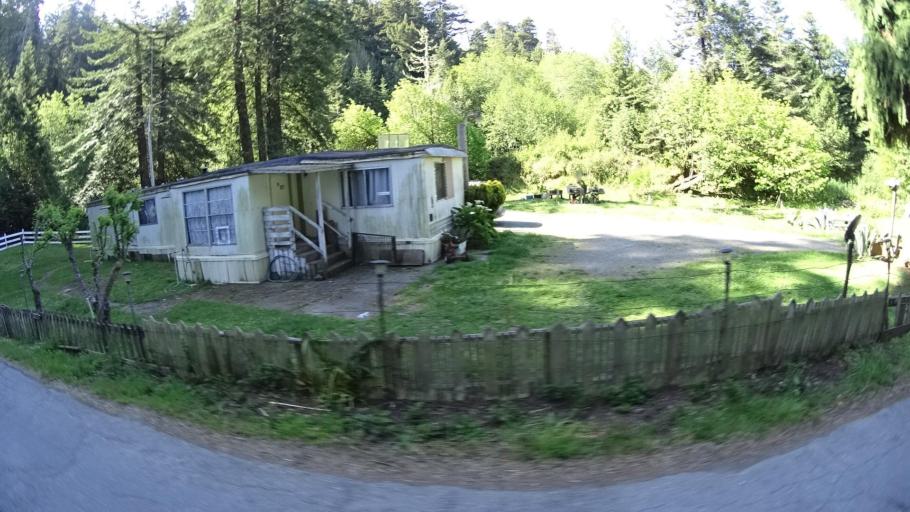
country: US
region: California
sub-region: Humboldt County
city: Rio Dell
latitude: 40.5281
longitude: -124.1702
